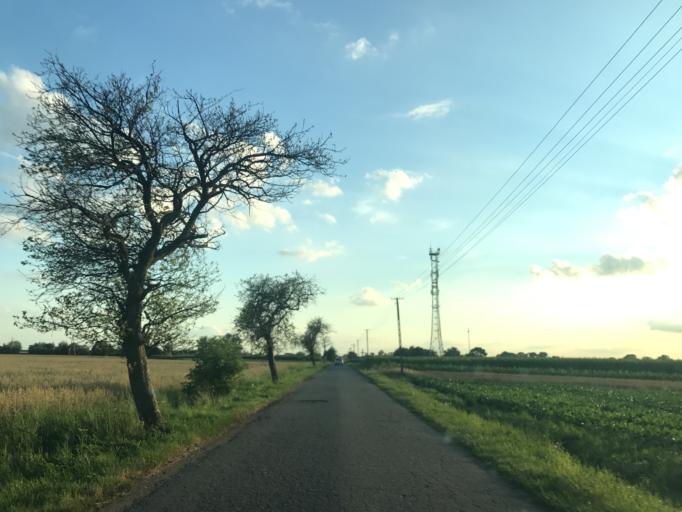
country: PL
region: Greater Poland Voivodeship
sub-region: Powiat gostynski
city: Piaski
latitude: 51.8151
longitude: 17.0639
